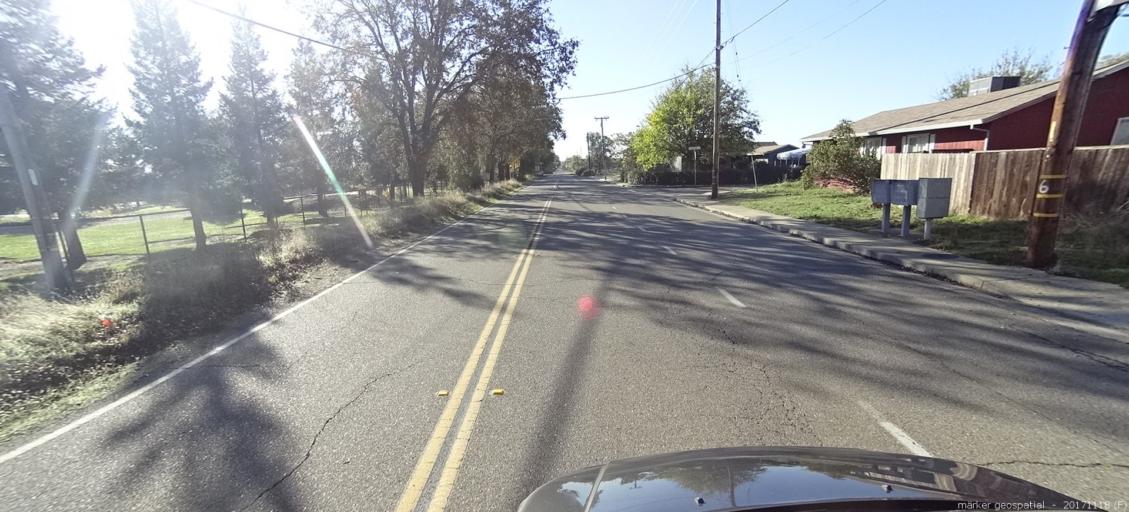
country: US
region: California
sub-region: Shasta County
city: Cottonwood
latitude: 40.3941
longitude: -122.2740
